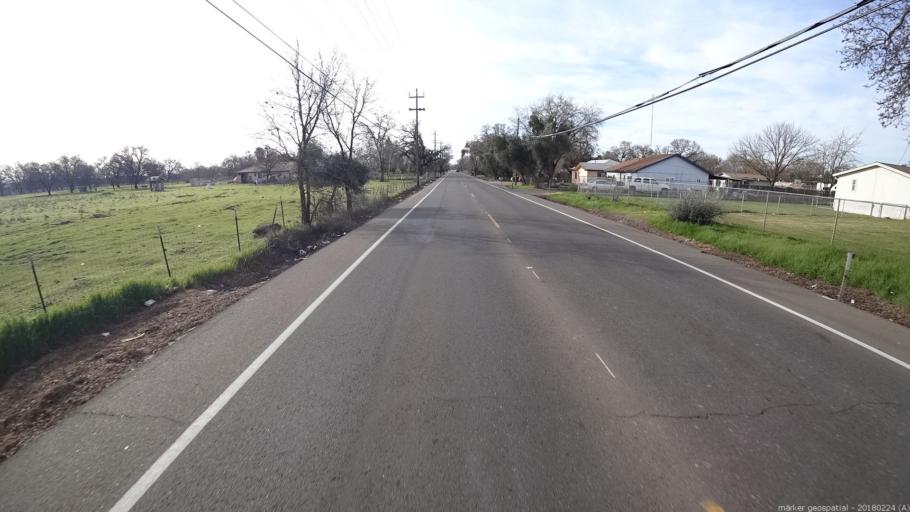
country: US
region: California
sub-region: Sacramento County
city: Rio Linda
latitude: 38.6794
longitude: -121.4569
